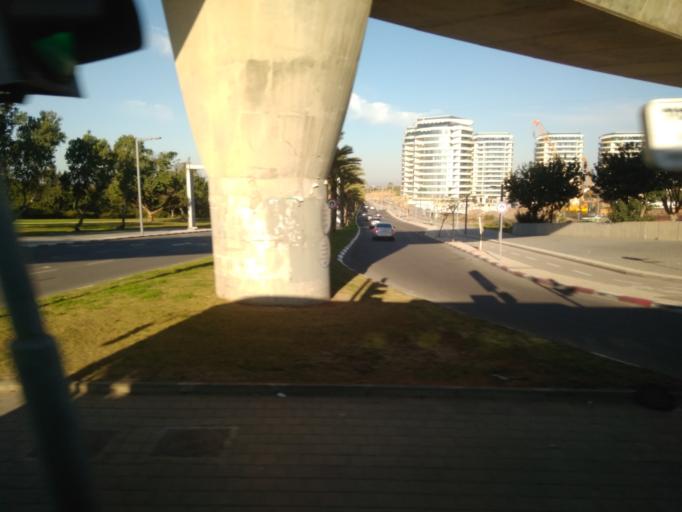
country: IL
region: Tel Aviv
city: Herzliya Pituah
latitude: 32.1410
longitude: 34.8012
